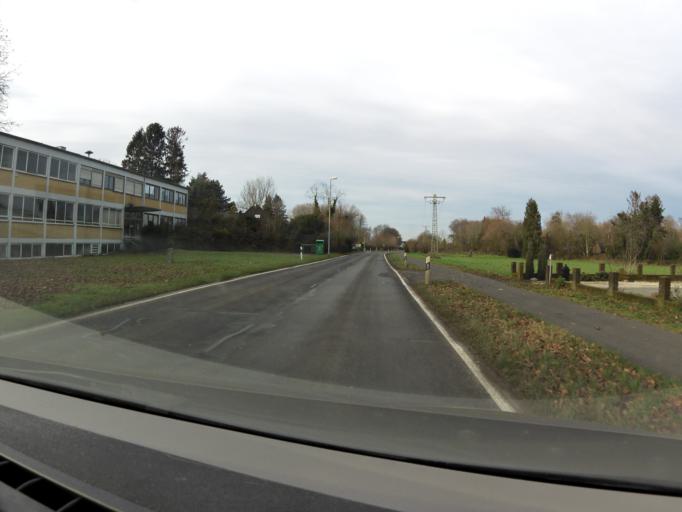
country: DE
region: North Rhine-Westphalia
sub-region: Regierungsbezirk Dusseldorf
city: Nettetal
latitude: 51.3072
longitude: 6.2440
